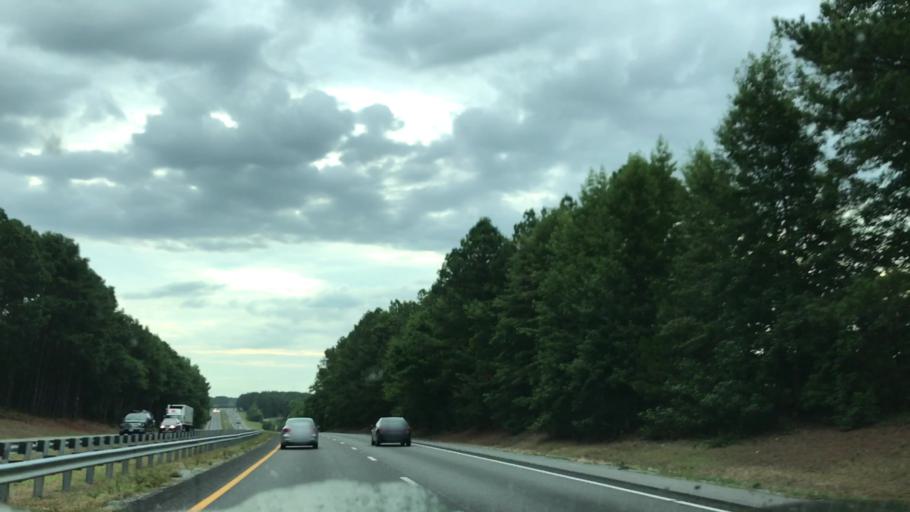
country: US
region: North Carolina
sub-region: Johnston County
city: Four Oaks
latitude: 35.4275
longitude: -78.4369
